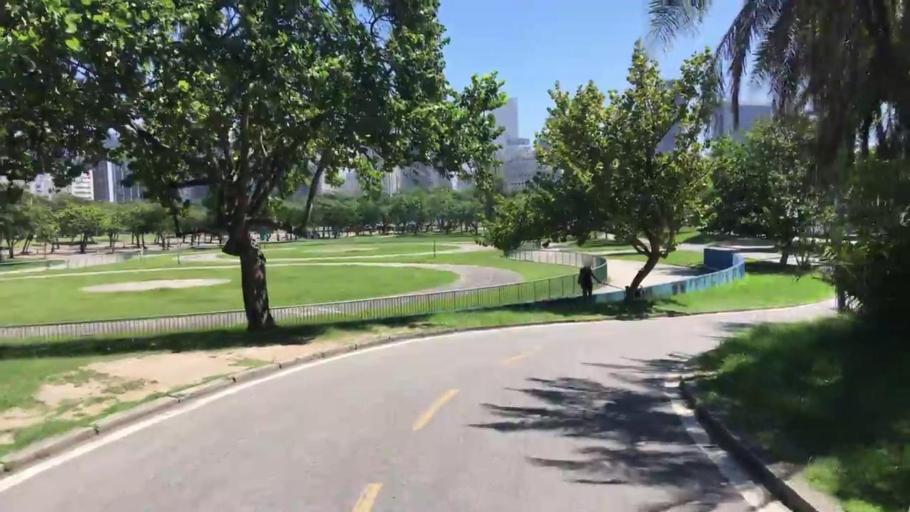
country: BR
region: Rio de Janeiro
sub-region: Rio De Janeiro
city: Rio de Janeiro
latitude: -22.9191
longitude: -43.1730
